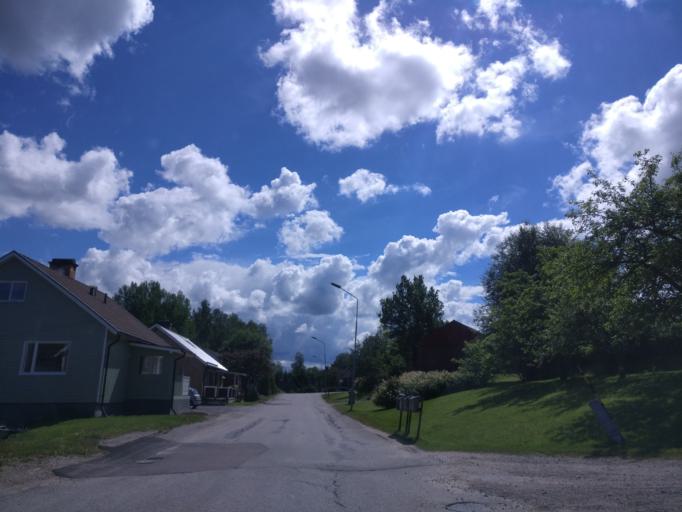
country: SE
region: Vaermland
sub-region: Hagfors Kommun
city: Hagfors
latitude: 60.0207
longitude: 13.6825
